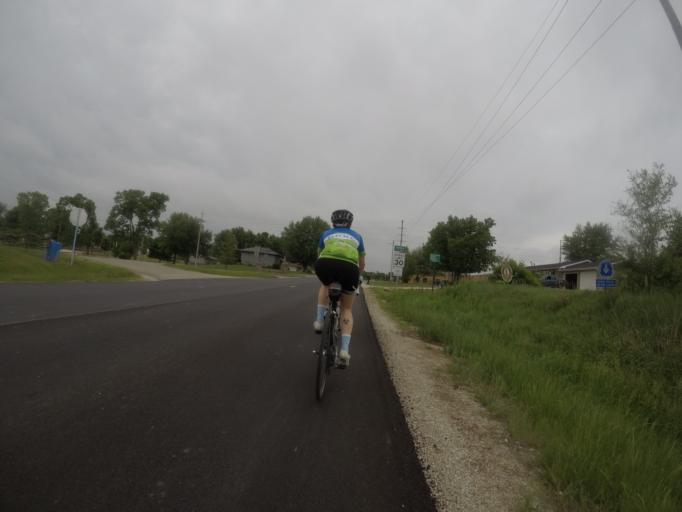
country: US
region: Kansas
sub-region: Pottawatomie County
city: Westmoreland
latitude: 39.4975
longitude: -96.1699
